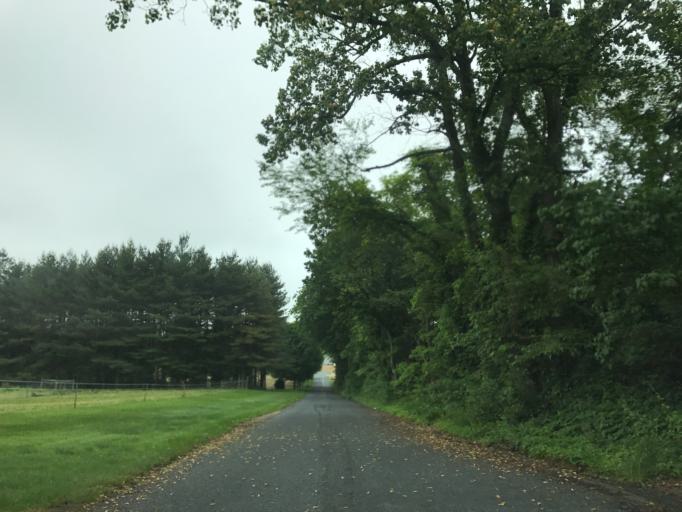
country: US
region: Pennsylvania
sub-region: York County
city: Stewartstown
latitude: 39.7089
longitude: -76.5056
